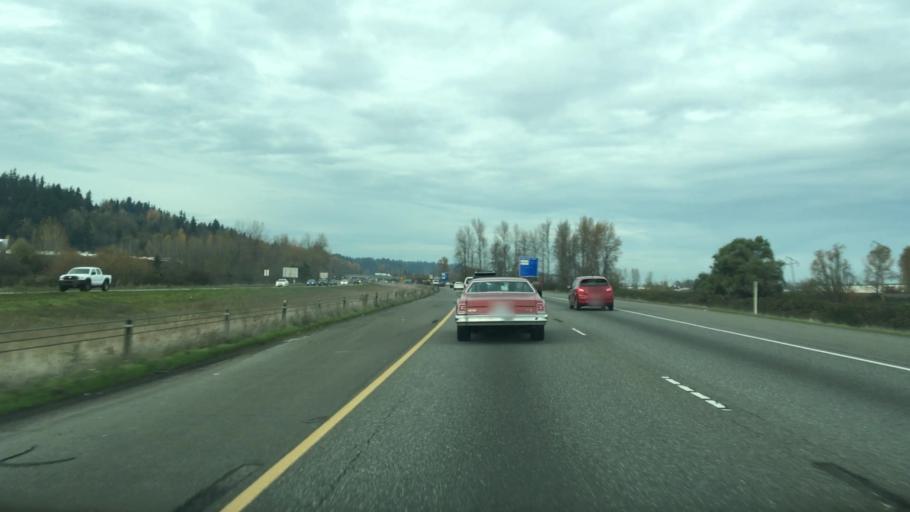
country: US
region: Washington
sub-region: Pierce County
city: Sumner
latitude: 47.2249
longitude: -122.2472
